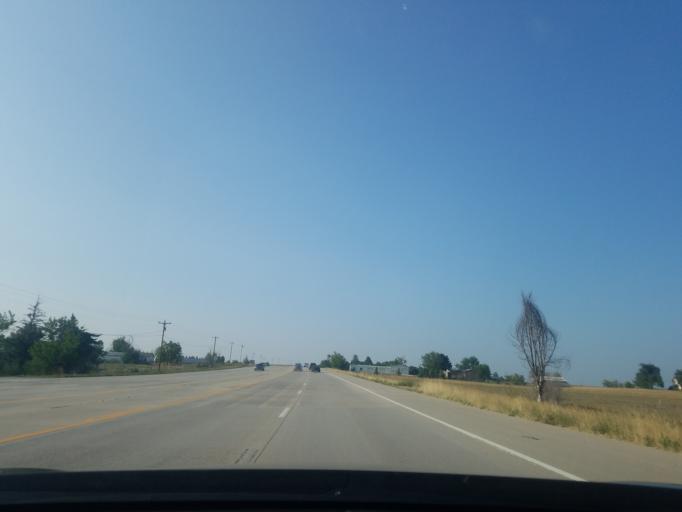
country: US
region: Colorado
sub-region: Boulder County
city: Longmont
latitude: 40.2357
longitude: -105.1023
